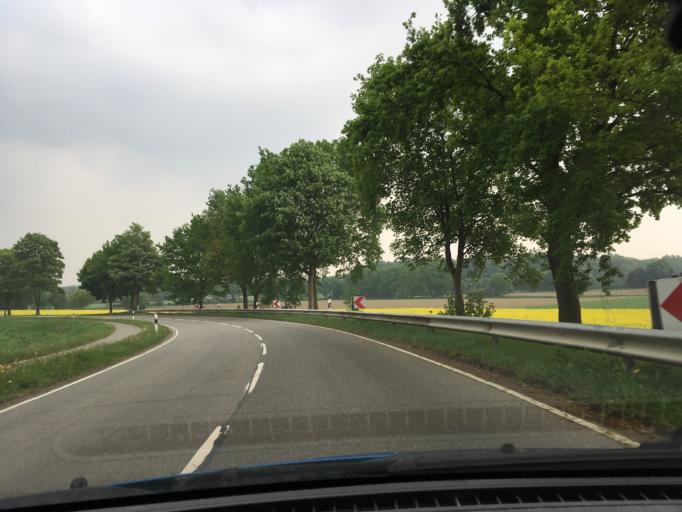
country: DE
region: Lower Saxony
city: Seevetal
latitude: 53.3881
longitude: 9.9514
